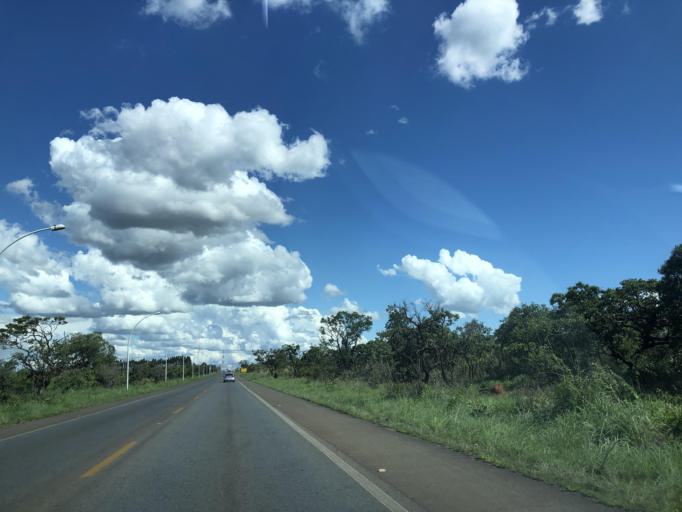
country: BR
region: Federal District
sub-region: Brasilia
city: Brasilia
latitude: -15.6793
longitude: -47.8712
